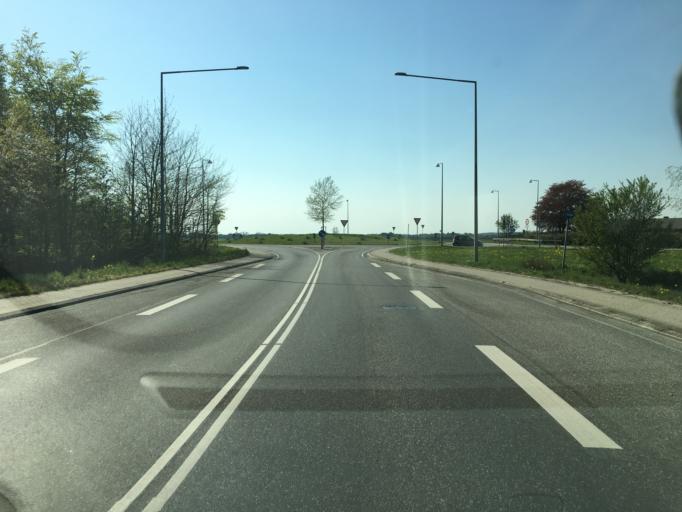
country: DK
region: South Denmark
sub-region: Haderslev Kommune
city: Vojens
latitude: 55.3104
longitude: 9.2828
